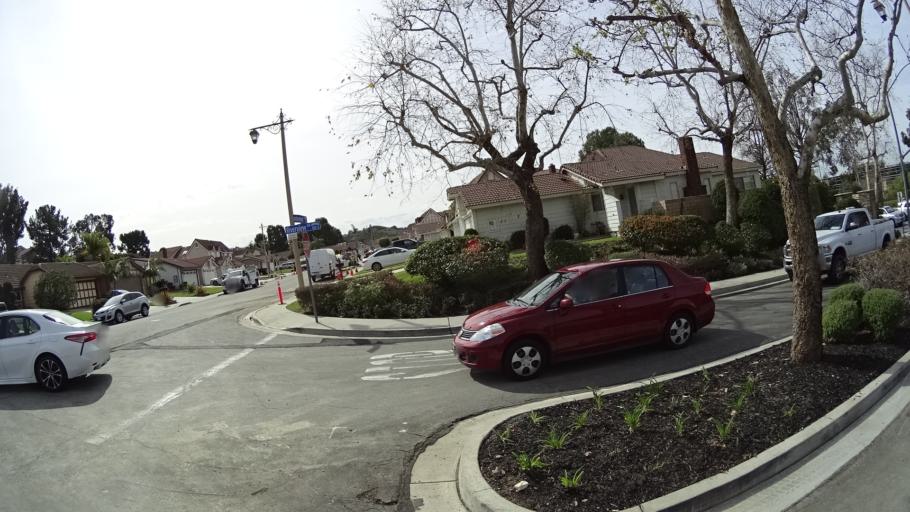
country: US
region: California
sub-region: Orange County
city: Yorba Linda
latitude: 33.8691
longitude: -117.7401
